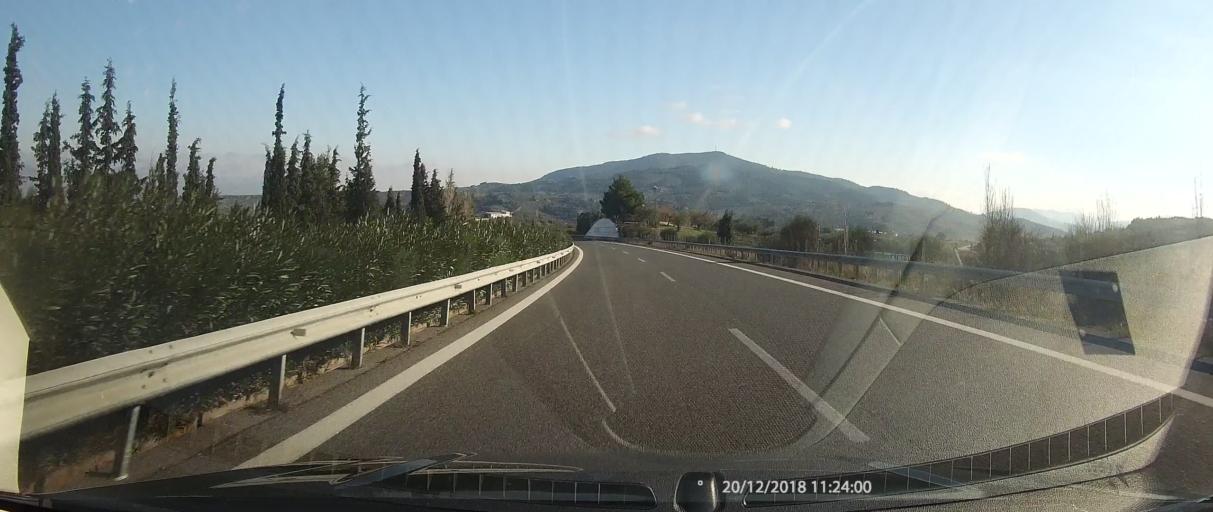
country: GR
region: Peloponnese
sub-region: Nomos Korinthias
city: Arkhaia Korinthos
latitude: 37.8728
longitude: 22.8720
